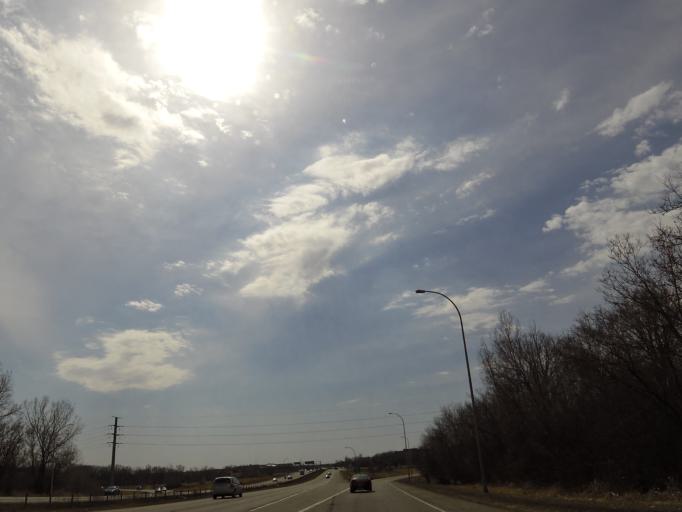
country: US
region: Minnesota
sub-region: Dakota County
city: South Saint Paul
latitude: 44.8797
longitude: -93.0610
